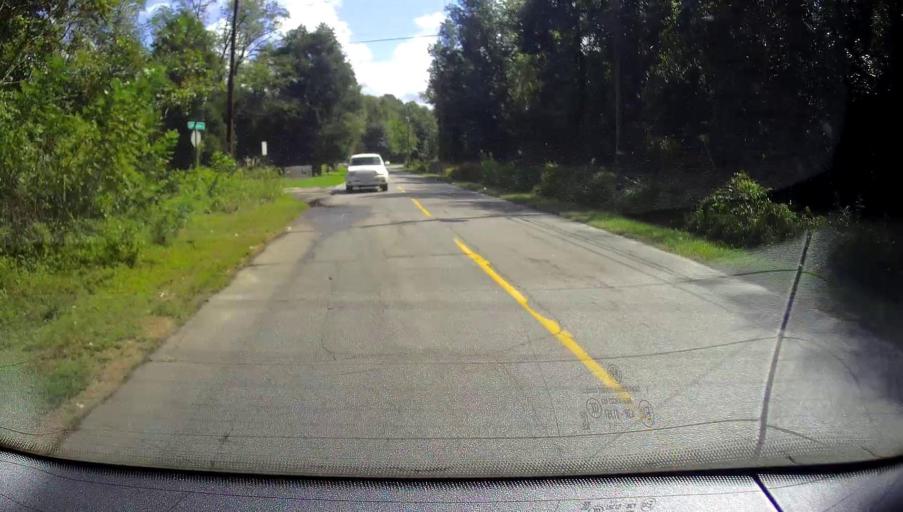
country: US
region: Georgia
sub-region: Bibb County
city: Macon
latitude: 32.8492
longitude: -83.5810
